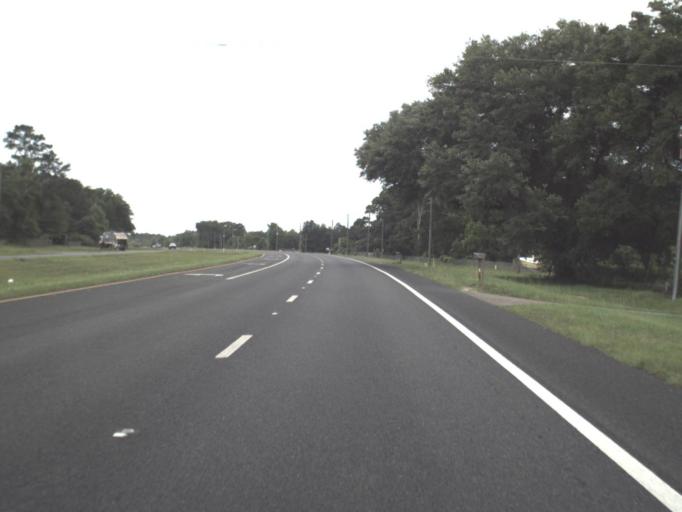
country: US
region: Florida
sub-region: Nassau County
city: Yulee
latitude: 30.6163
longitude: -81.7124
